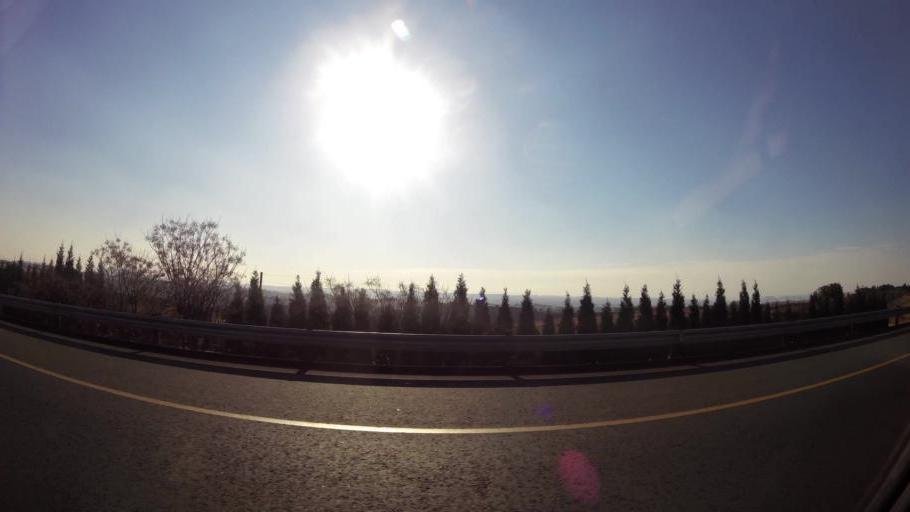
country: ZA
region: Gauteng
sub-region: West Rand District Municipality
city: Muldersdriseloop
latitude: -25.9914
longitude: 27.9141
